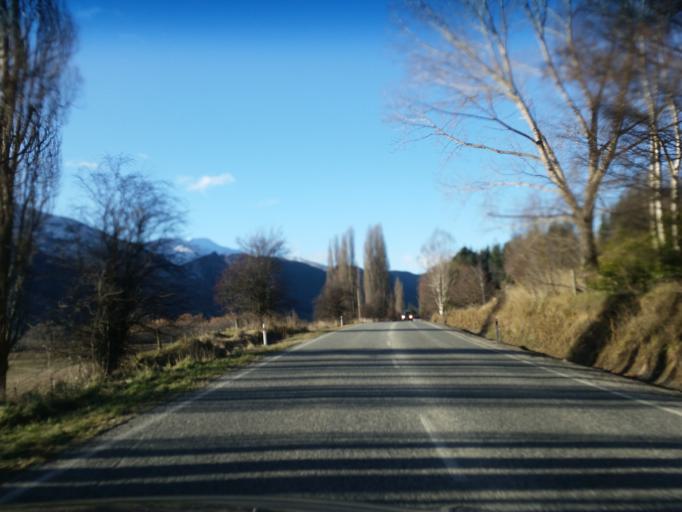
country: NZ
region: Otago
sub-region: Queenstown-Lakes District
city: Arrowtown
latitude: -44.9593
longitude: 168.7268
